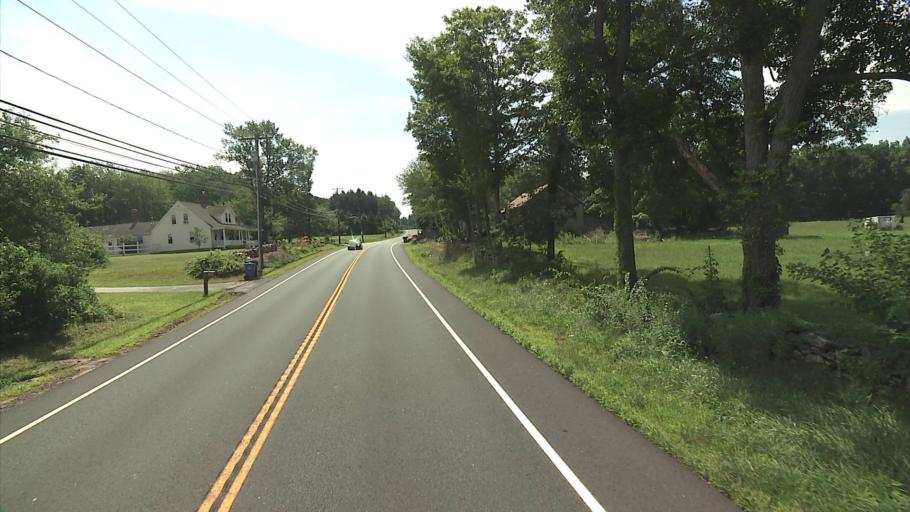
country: US
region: Connecticut
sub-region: Tolland County
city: Rockville
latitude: 41.8435
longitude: -72.4182
